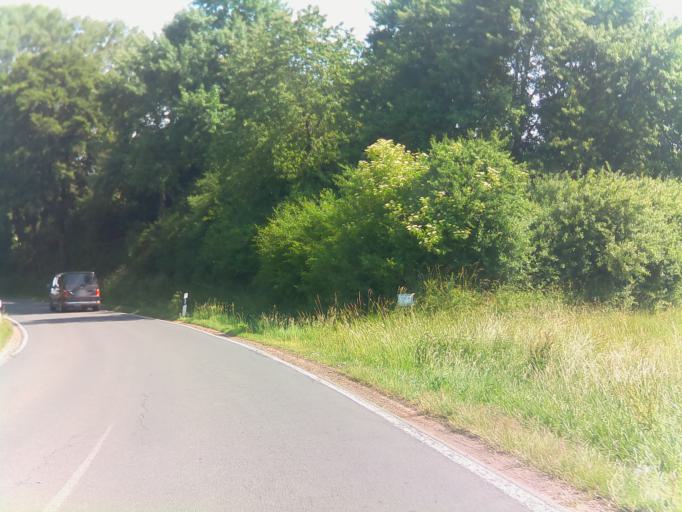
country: DE
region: Hesse
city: Rosenthal
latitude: 50.9660
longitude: 8.8716
